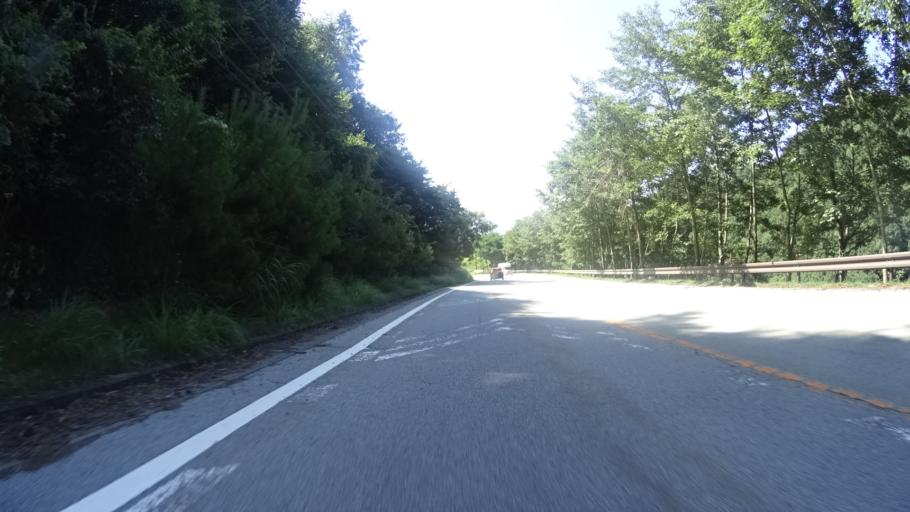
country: JP
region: Yamanashi
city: Enzan
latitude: 35.7556
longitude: 138.8078
